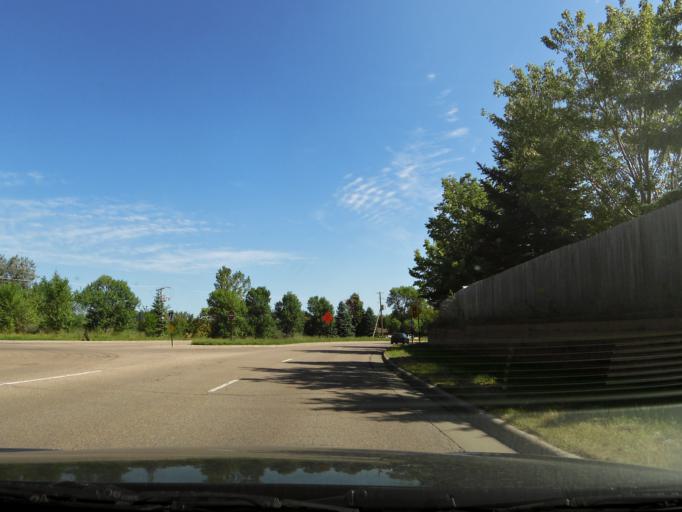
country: US
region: Minnesota
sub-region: Hennepin County
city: Minnetonka
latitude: 44.8909
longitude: -93.5203
